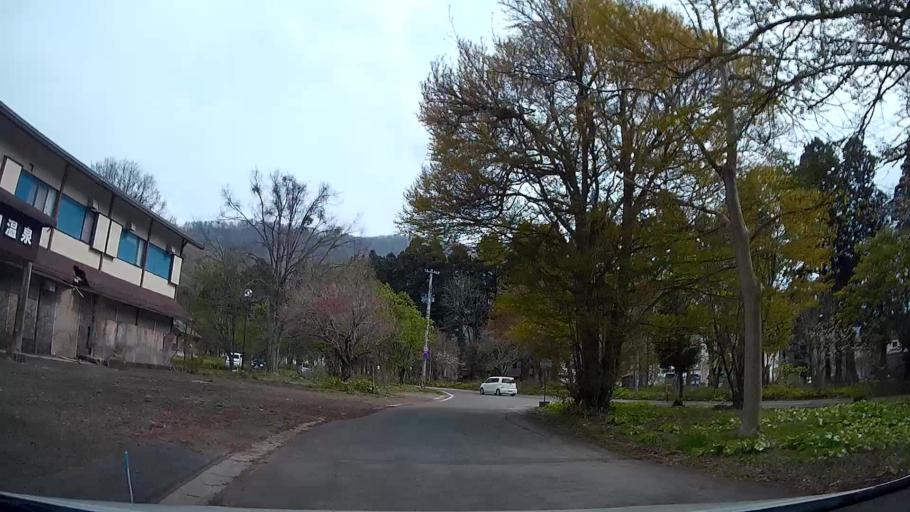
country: JP
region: Akita
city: Hanawa
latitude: 40.4273
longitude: 140.8953
